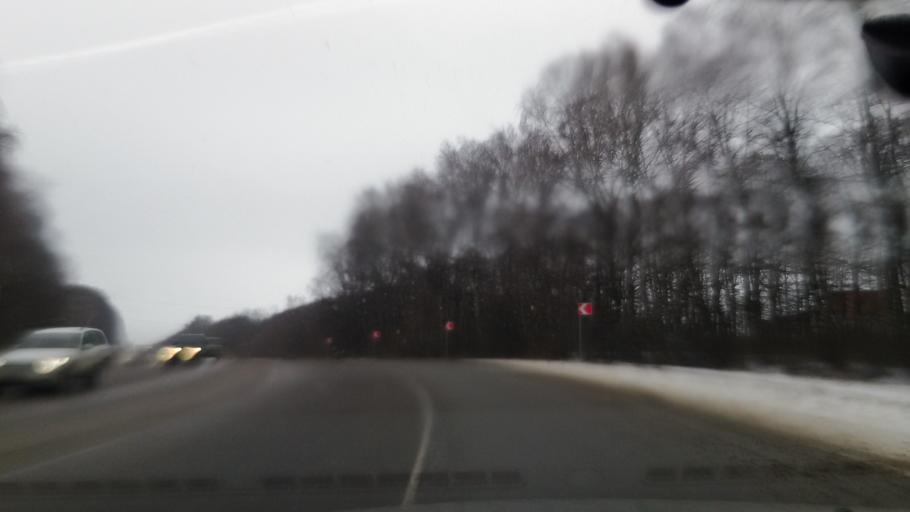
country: RU
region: Tula
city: Skuratovskiy
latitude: 54.1267
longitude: 37.6829
